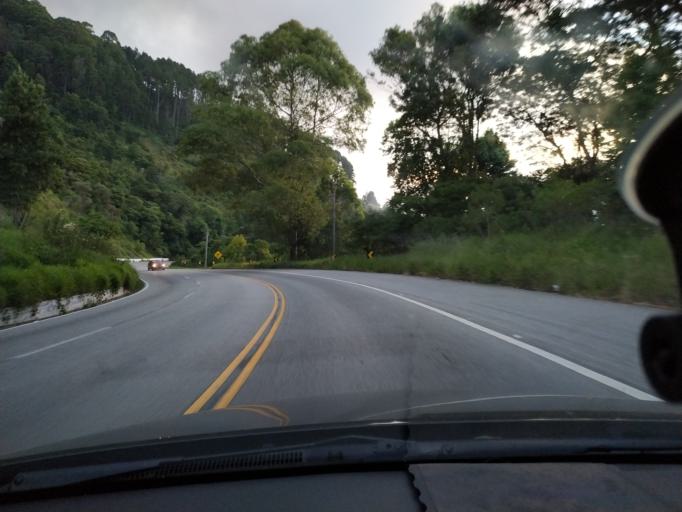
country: BR
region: Sao Paulo
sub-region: Campos Do Jordao
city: Campos do Jordao
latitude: -22.7899
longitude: -45.6205
